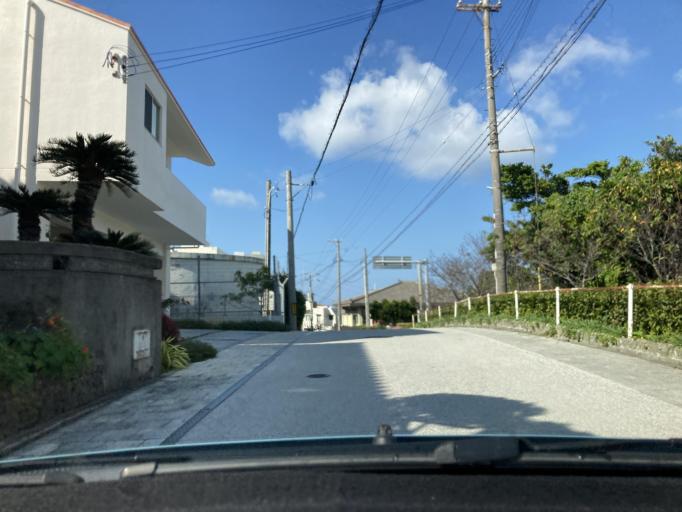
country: JP
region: Okinawa
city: Ginowan
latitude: 26.2485
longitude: 127.7298
